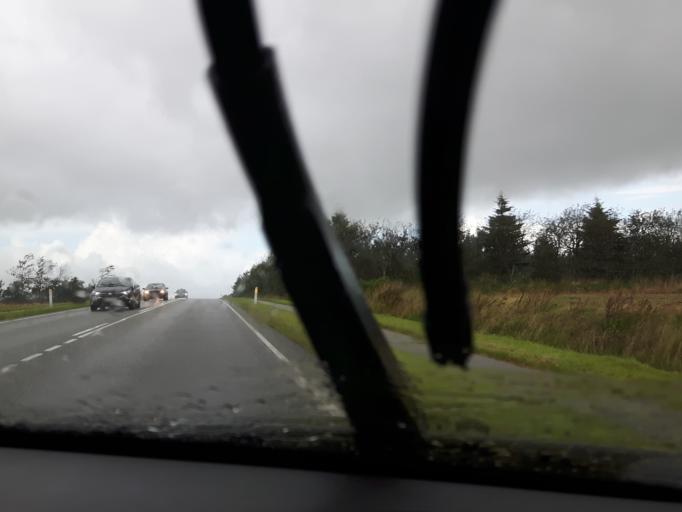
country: DK
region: North Denmark
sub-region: Jammerbugt Kommune
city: Fjerritslev
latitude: 57.0878
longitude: 9.3072
